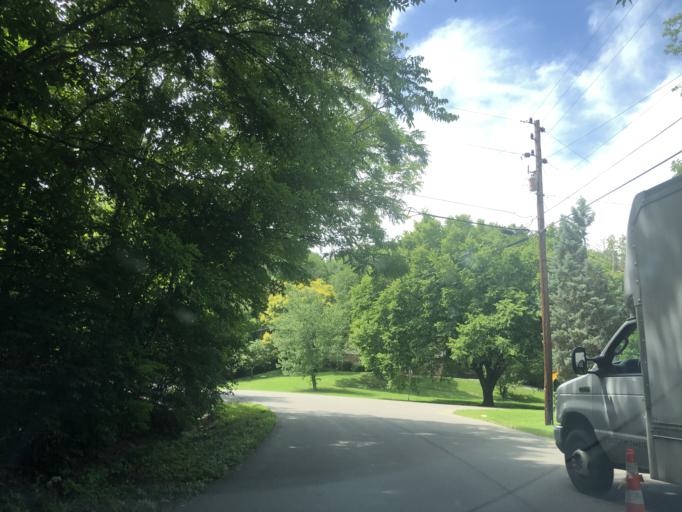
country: US
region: Tennessee
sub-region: Davidson County
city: Belle Meade
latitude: 36.0779
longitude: -86.9337
